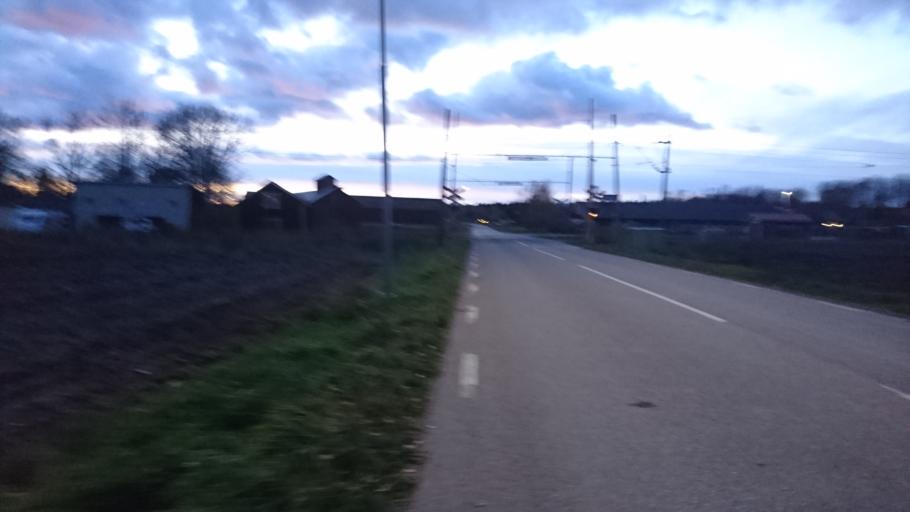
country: SE
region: Vaestmanland
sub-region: Sala Kommun
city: Sala
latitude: 59.8063
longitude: 16.6418
